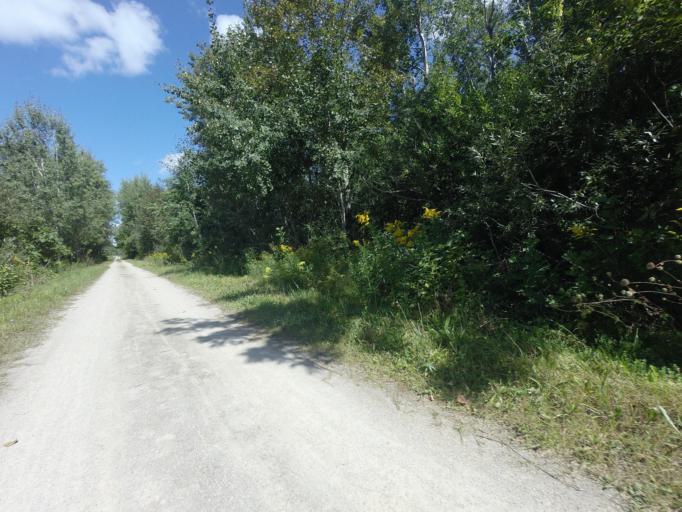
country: CA
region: Ontario
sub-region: Wellington County
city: Guelph
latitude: 43.7588
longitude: -80.3233
